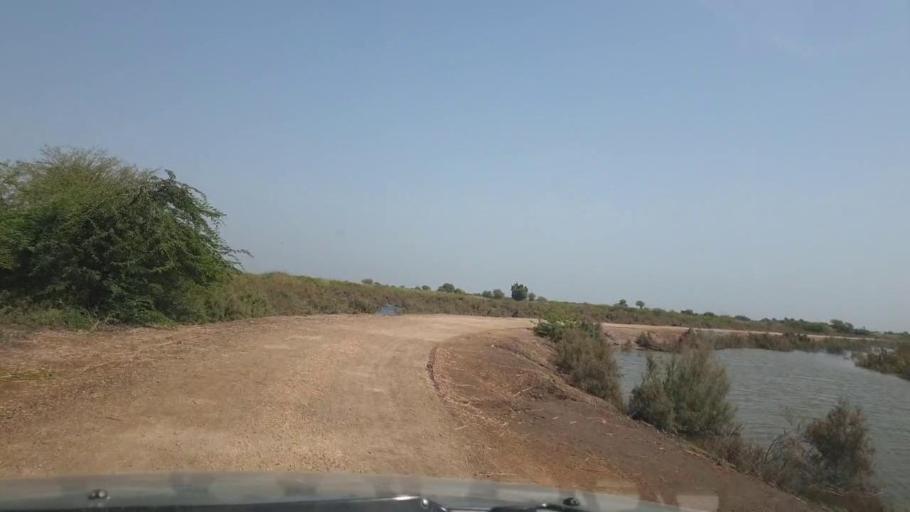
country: PK
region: Sindh
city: Tando Ghulam Ali
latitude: 25.1037
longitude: 68.7960
